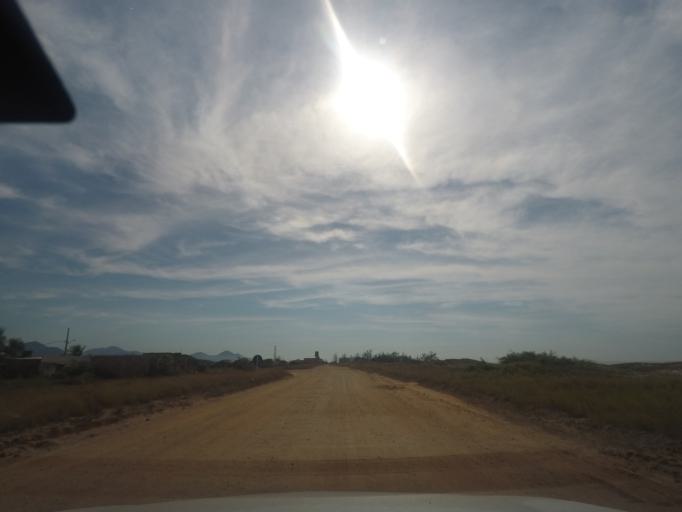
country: BR
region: Rio de Janeiro
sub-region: Marica
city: Marica
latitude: -22.9593
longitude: -42.8329
